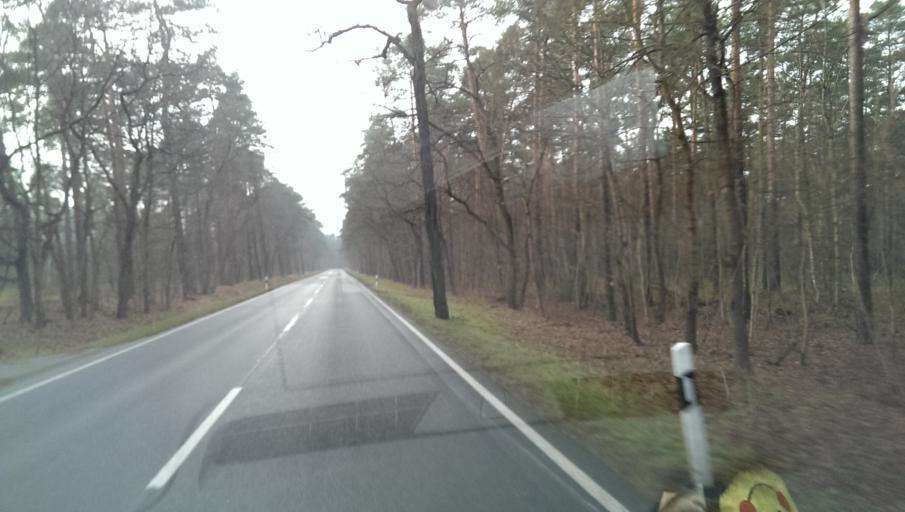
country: DE
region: Brandenburg
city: Luckenwalde
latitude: 52.0560
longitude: 13.1477
